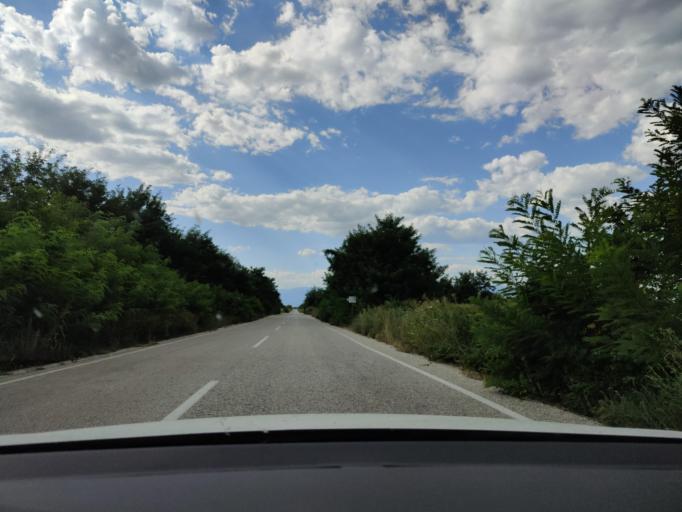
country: GR
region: Central Macedonia
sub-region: Nomos Serron
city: Strymoniko
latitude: 41.0690
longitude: 23.3030
